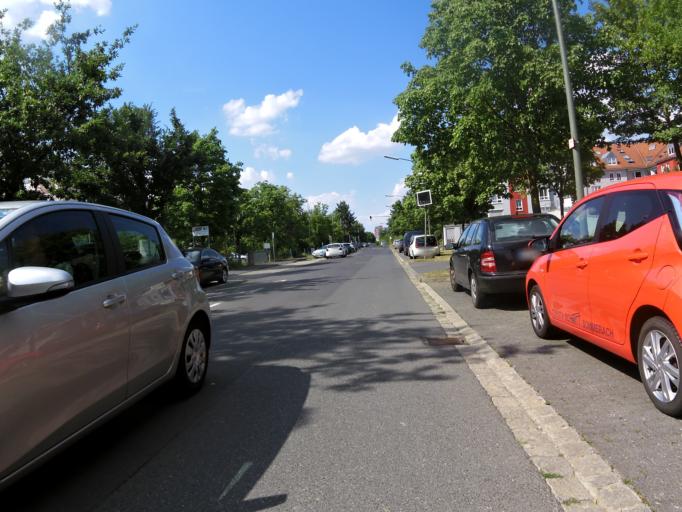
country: DE
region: Bavaria
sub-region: Regierungsbezirk Unterfranken
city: Randersacker
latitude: 49.7420
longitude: 9.9563
